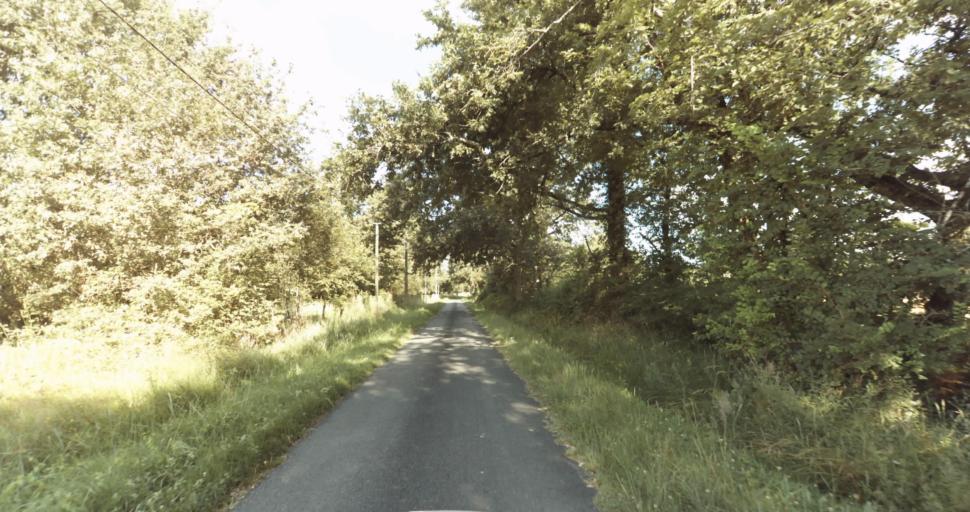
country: FR
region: Aquitaine
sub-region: Departement de la Gironde
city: Bazas
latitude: 44.4268
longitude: -0.2477
